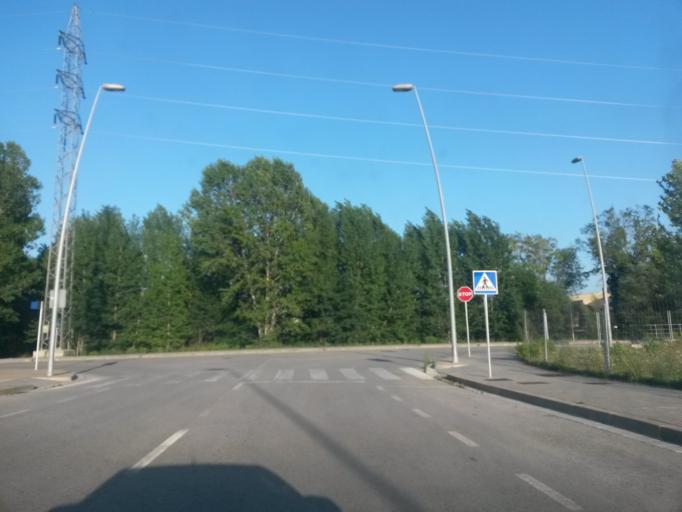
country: ES
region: Catalonia
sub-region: Provincia de Girona
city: Fornells de la Selva
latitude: 41.9500
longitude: 2.8016
